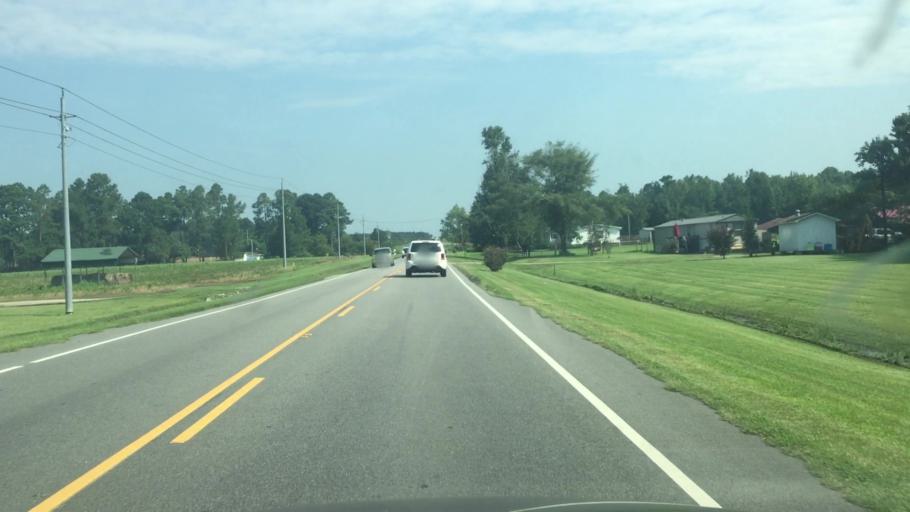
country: US
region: North Carolina
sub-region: Columbus County
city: Chadbourn
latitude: 34.3529
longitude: -78.8292
